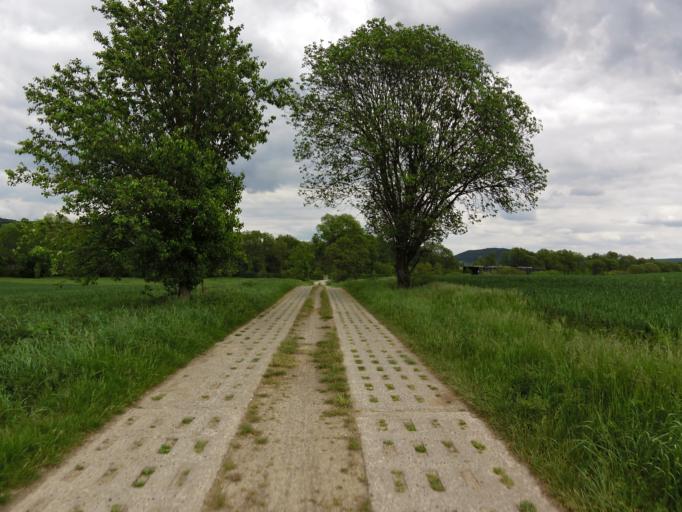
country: DE
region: Thuringia
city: Creuzburg
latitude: 51.0496
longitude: 10.2146
